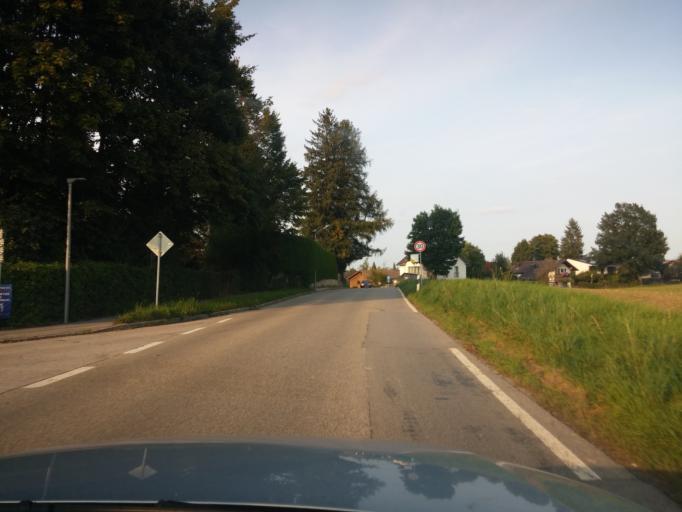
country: DE
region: Bavaria
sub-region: Upper Bavaria
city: Oberpframmern
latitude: 48.0186
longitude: 11.8112
